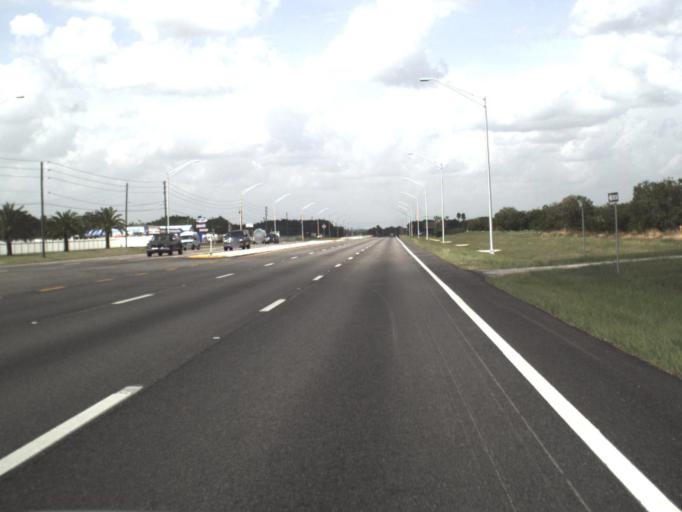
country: US
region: Florida
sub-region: Highlands County
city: Avon Park
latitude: 27.6382
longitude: -81.5222
